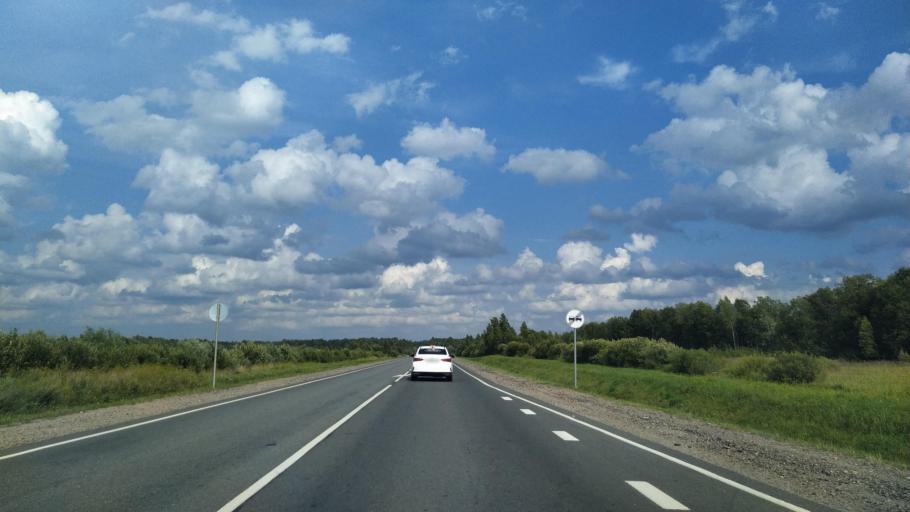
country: RU
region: Novgorod
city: Sol'tsy
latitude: 58.1358
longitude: 30.3927
